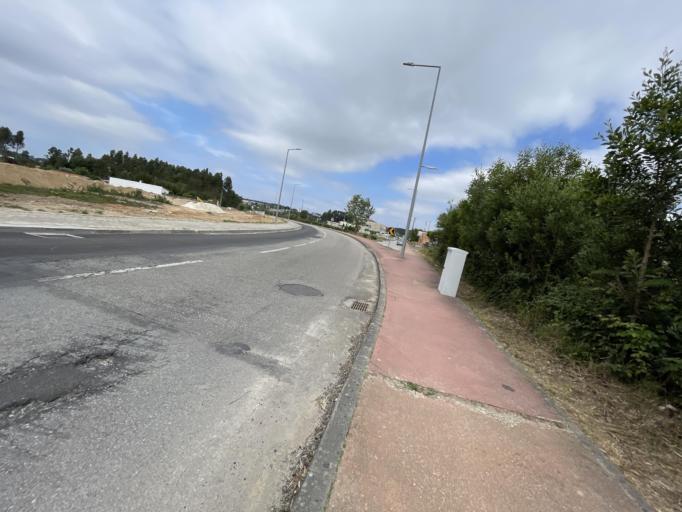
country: PT
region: Aveiro
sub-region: Ovar
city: Cortegaca
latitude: 40.9413
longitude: -8.6360
